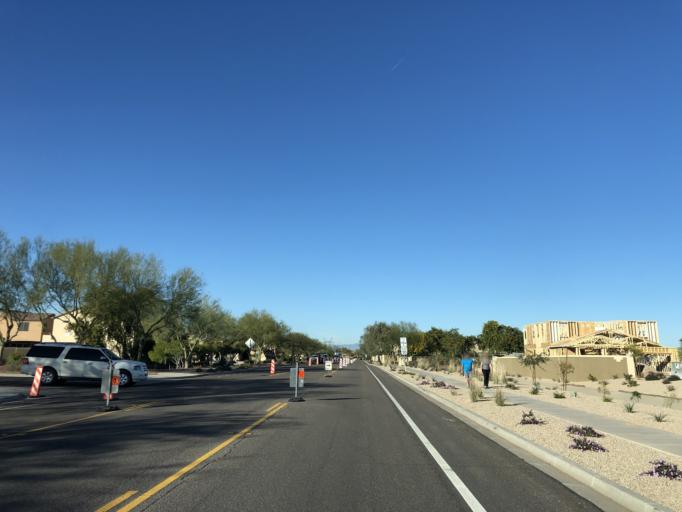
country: US
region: Arizona
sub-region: Maricopa County
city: Sun City West
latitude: 33.6902
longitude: -112.3251
